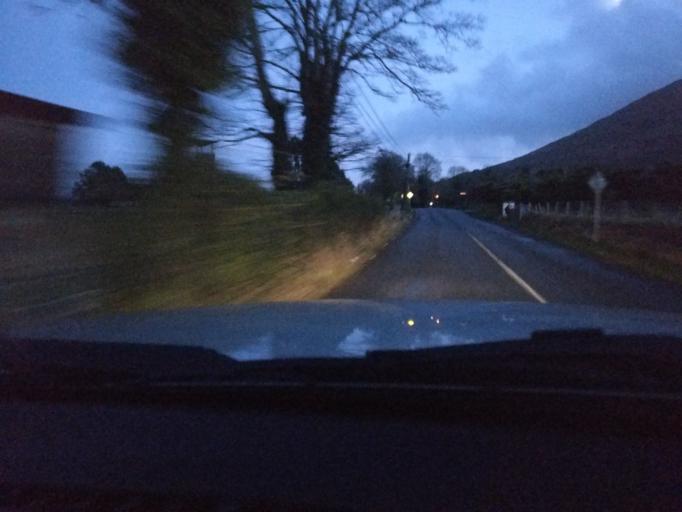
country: GB
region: Northern Ireland
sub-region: Down District
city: Warrenpoint
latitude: 54.0748
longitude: -6.2427
